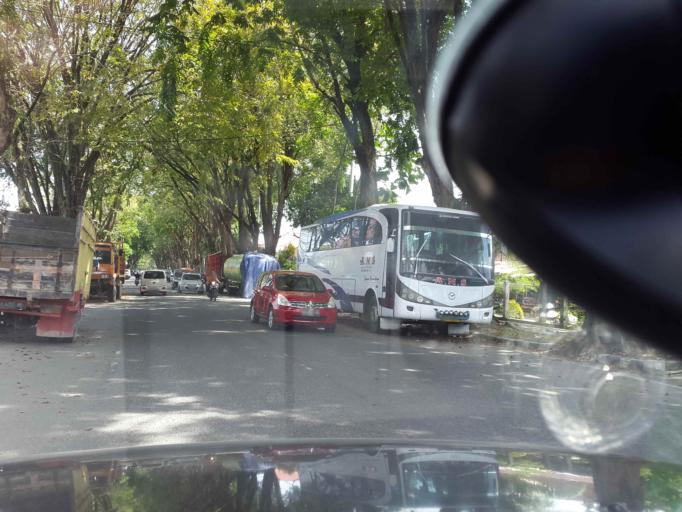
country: ID
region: West Sumatra
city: Padang
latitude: -0.9340
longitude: 100.3658
